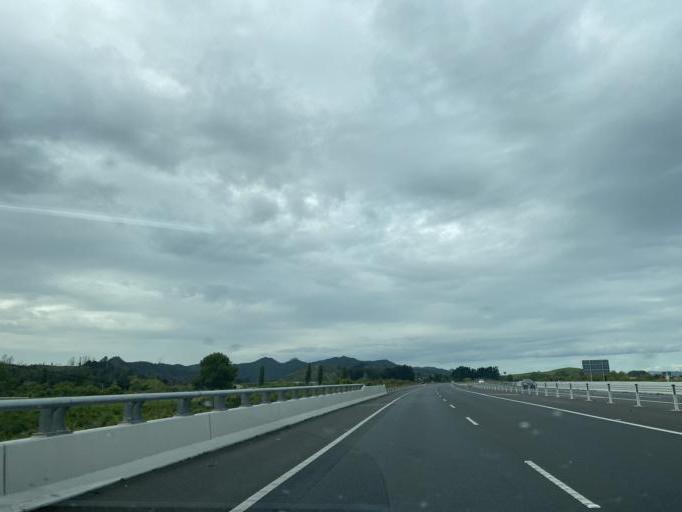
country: NZ
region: Waikato
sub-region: Waikato District
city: Ngaruawahia
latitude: -37.6062
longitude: 175.2051
